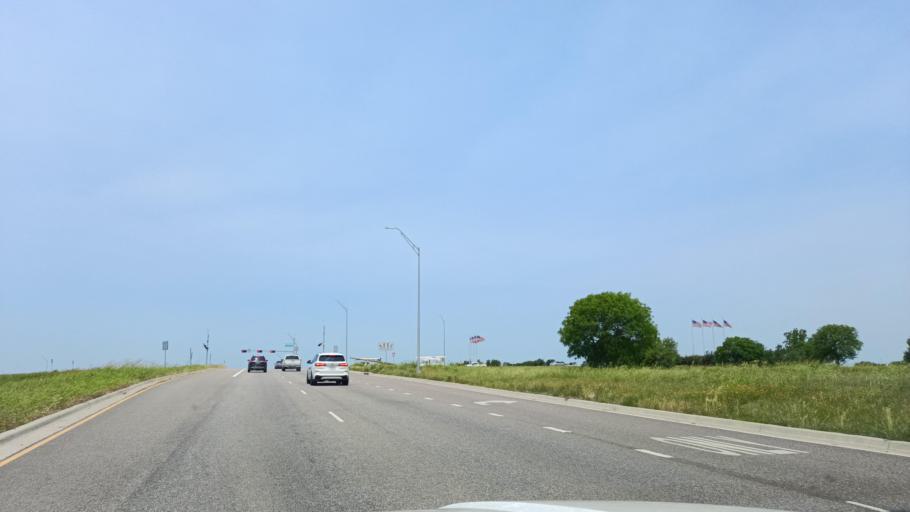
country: US
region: Texas
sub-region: Bell County
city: Temple
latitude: 31.0682
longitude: -97.3476
